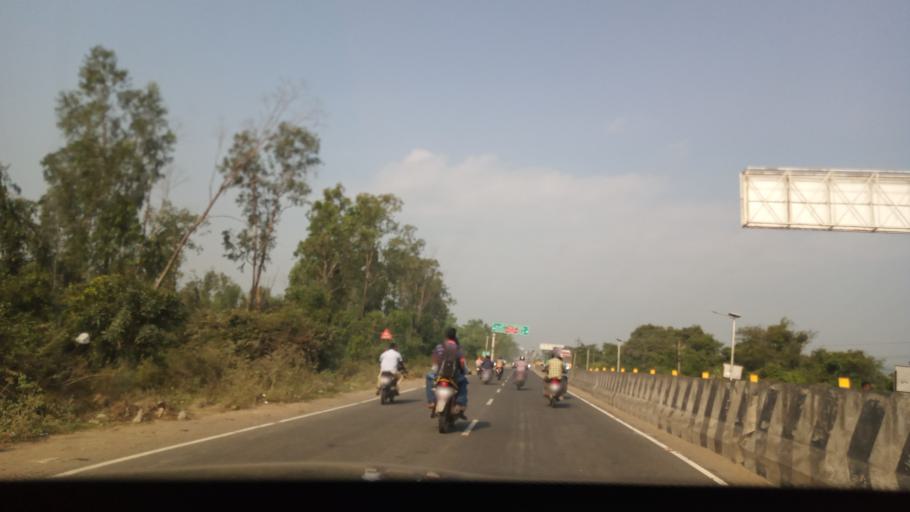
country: IN
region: Tamil Nadu
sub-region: Kancheepuram
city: Vandalur
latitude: 12.8628
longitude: 80.1267
